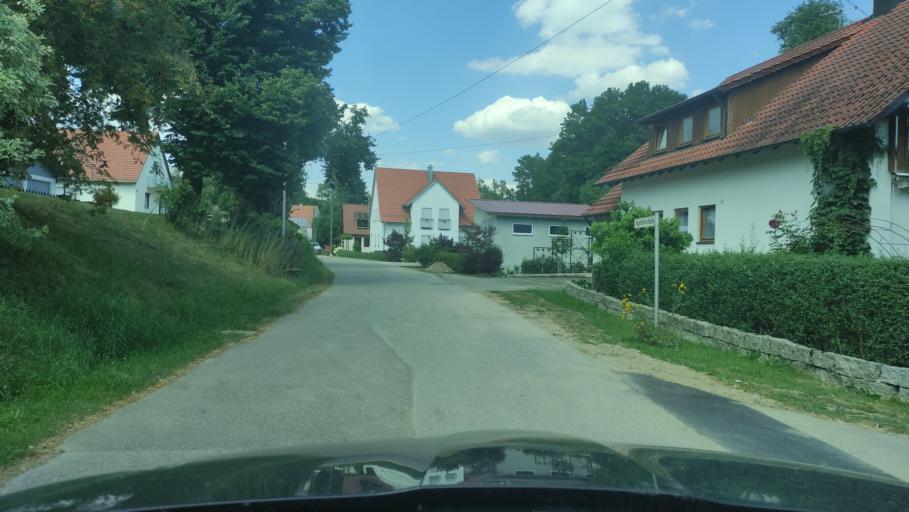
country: DE
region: Bavaria
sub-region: Swabia
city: Deisenhausen
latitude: 48.2881
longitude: 10.3008
